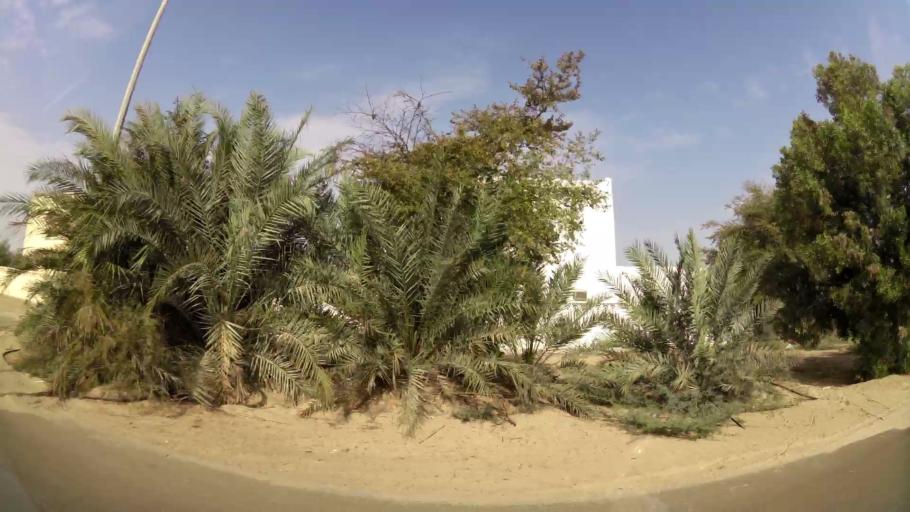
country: AE
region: Abu Dhabi
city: Abu Dhabi
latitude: 24.2614
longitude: 54.6739
